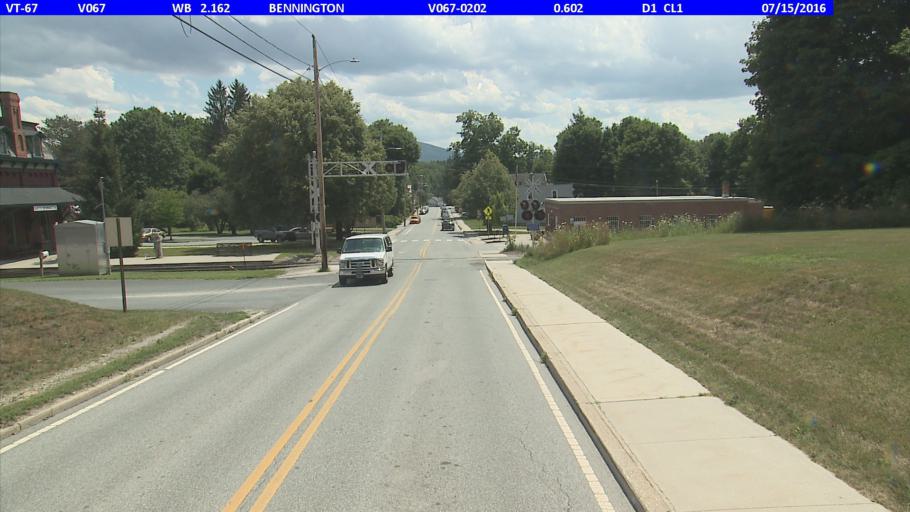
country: US
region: Vermont
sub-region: Bennington County
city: North Bennington
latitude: 42.9327
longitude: -73.2427
